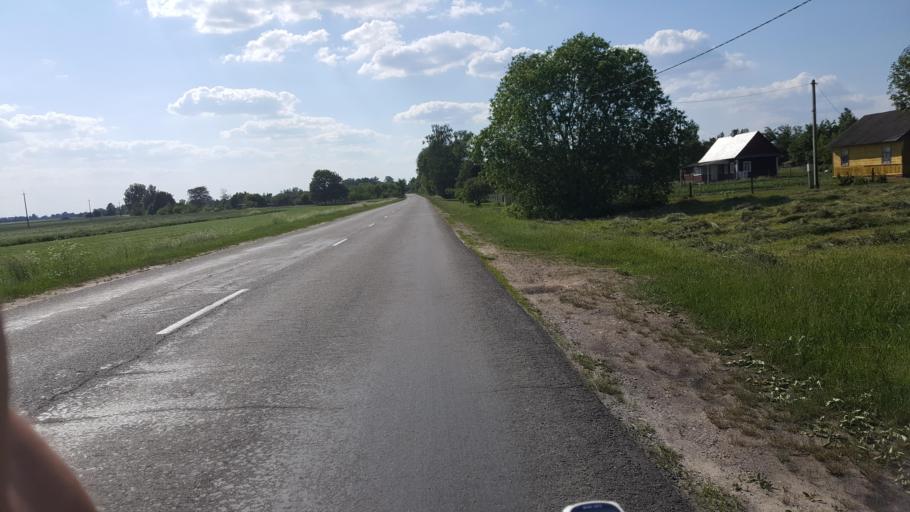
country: BY
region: Brest
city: Kobryn
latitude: 52.3452
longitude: 24.2181
